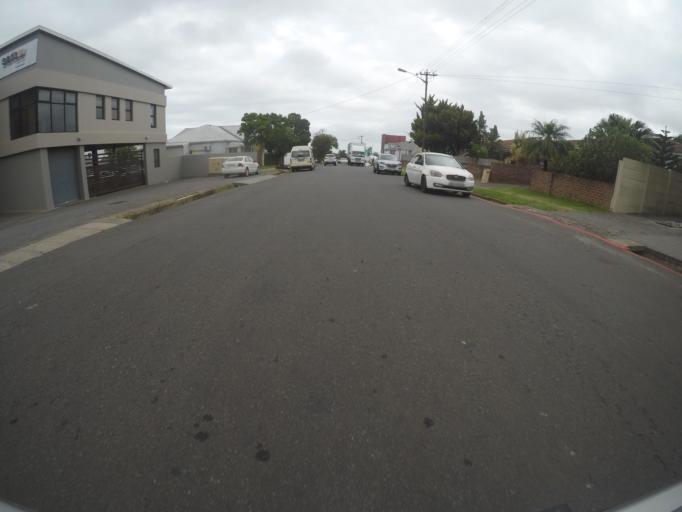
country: ZA
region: Eastern Cape
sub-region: Buffalo City Metropolitan Municipality
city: East London
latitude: -32.9796
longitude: 27.9015
